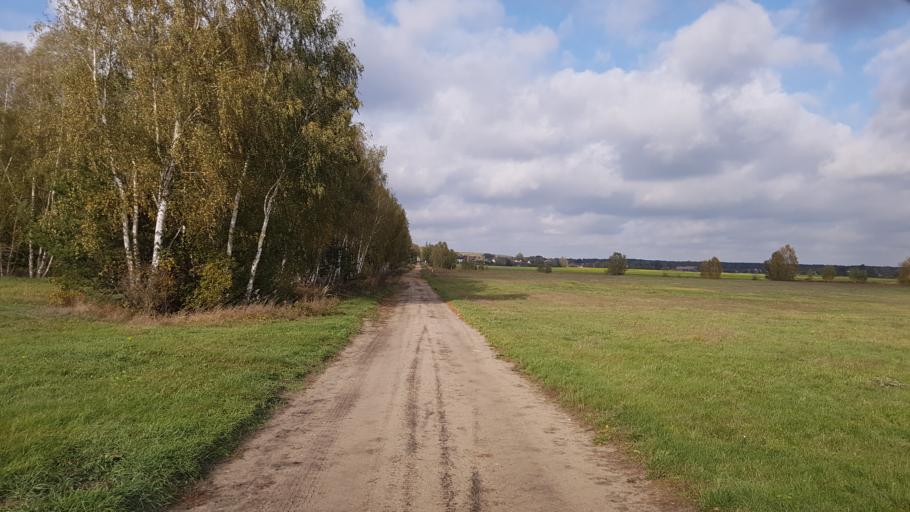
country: DE
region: Brandenburg
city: Schonborn
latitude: 51.5848
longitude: 13.4932
